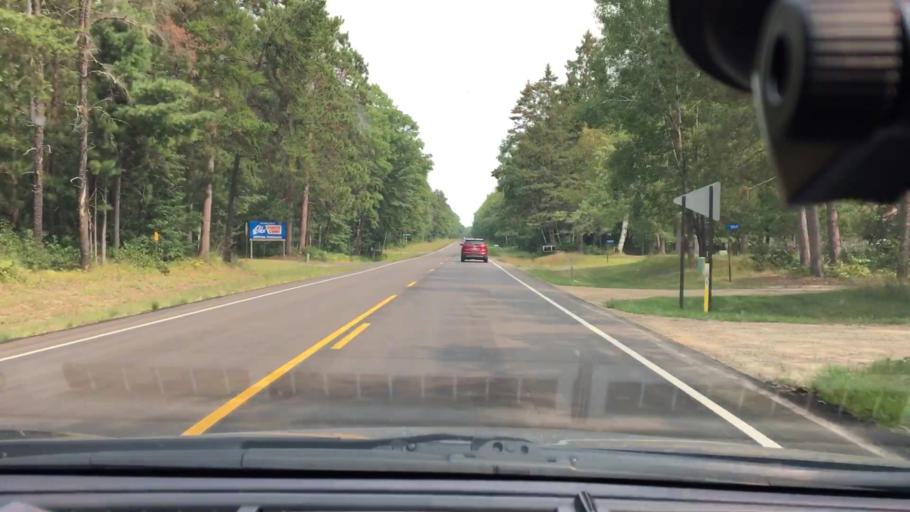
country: US
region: Minnesota
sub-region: Crow Wing County
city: Breezy Point
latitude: 46.5335
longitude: -94.1789
